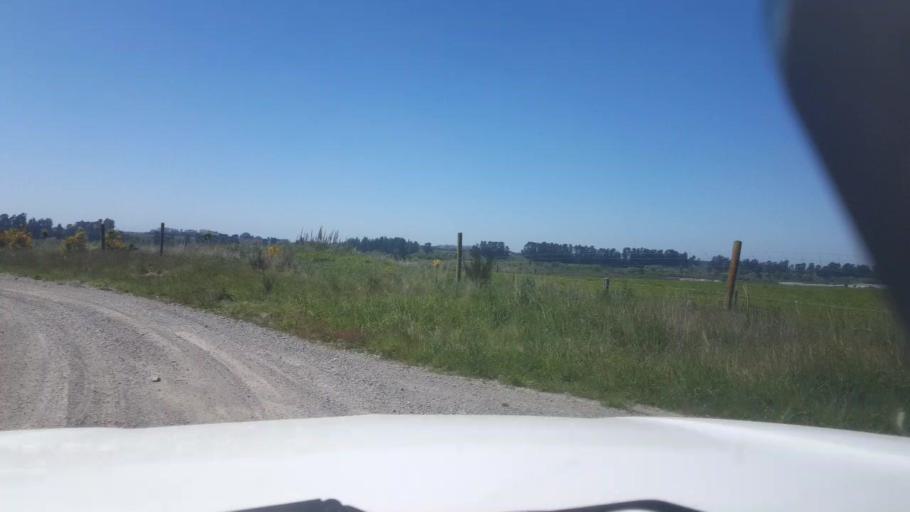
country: NZ
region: Canterbury
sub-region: Timaru District
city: Pleasant Point
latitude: -43.9451
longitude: 171.2814
